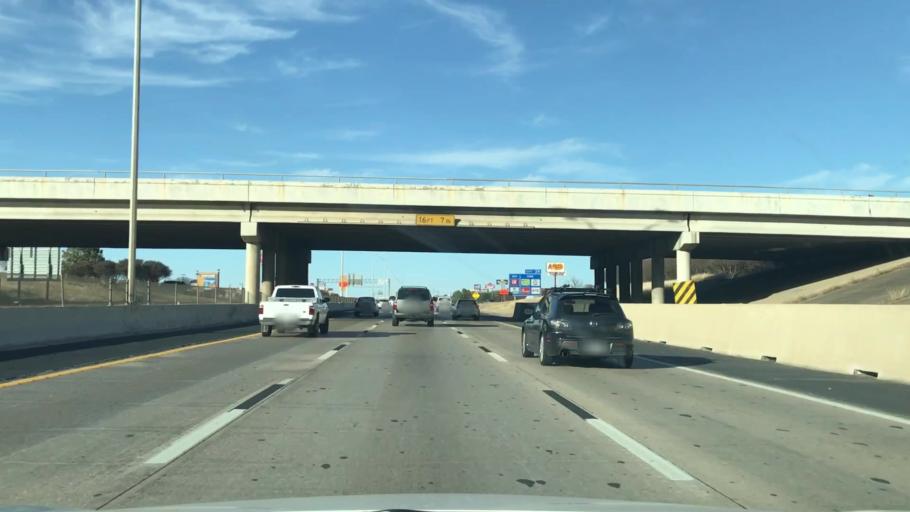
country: US
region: Texas
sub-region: Johnson County
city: Burleson
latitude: 32.5627
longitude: -97.3188
